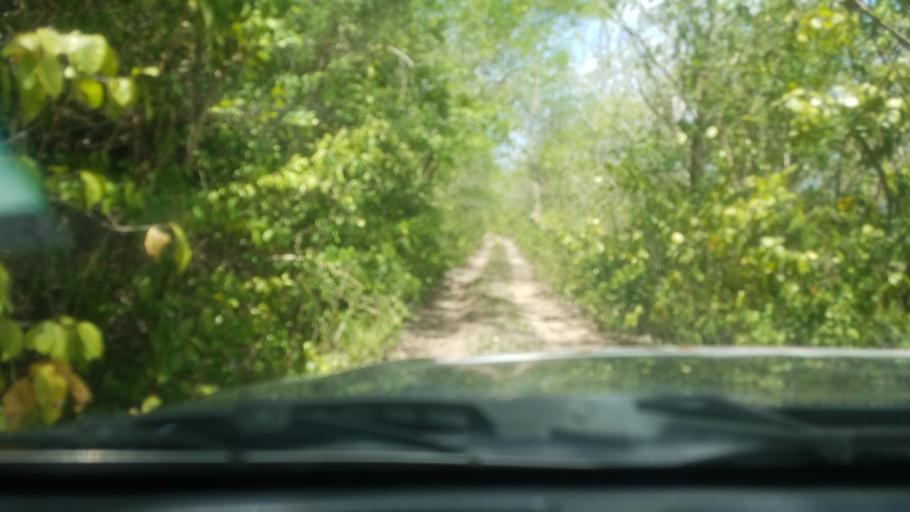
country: LC
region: Vieux-Fort
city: Vieux Fort
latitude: 13.7127
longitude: -60.9541
